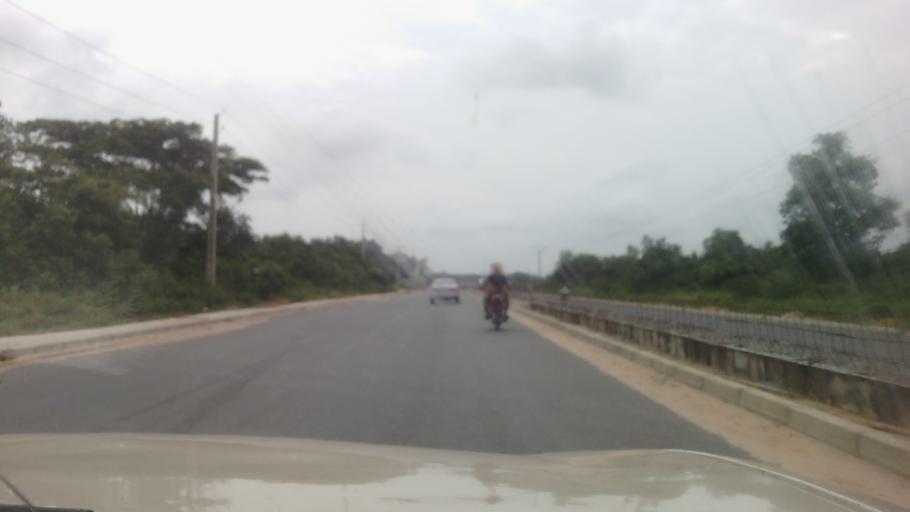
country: BJ
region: Atlantique
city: Ouidah
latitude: 6.3782
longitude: 2.1599
